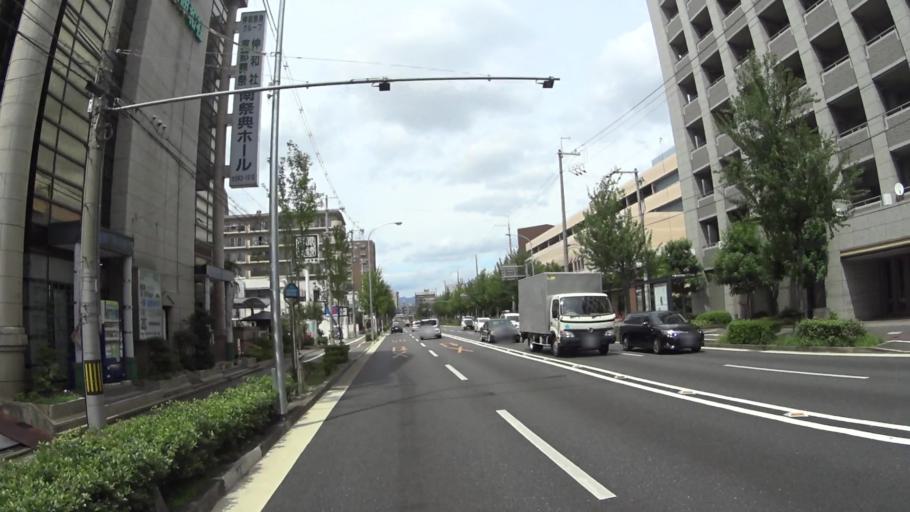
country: JP
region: Kyoto
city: Muko
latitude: 34.9739
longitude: 135.7359
